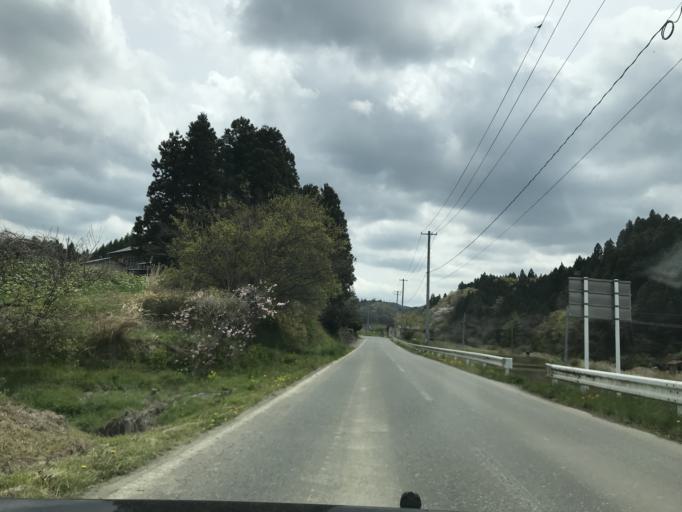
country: JP
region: Iwate
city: Ichinoseki
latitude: 38.8530
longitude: 141.3344
